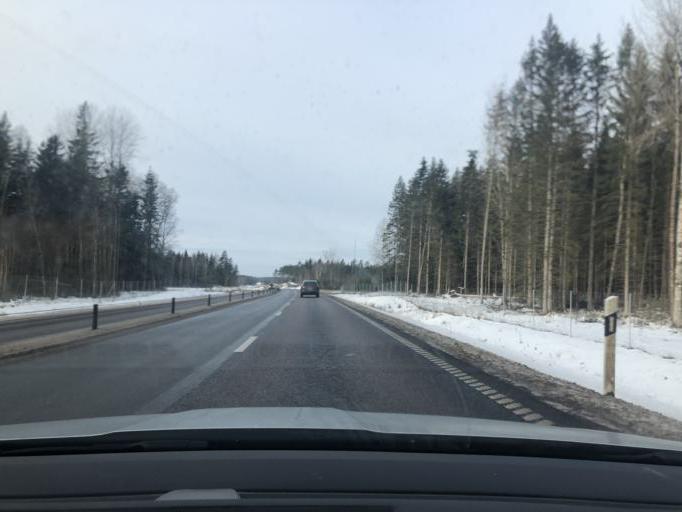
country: SE
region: OEstergoetland
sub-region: Motala Kommun
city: Ryd
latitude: 58.5894
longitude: 15.1670
